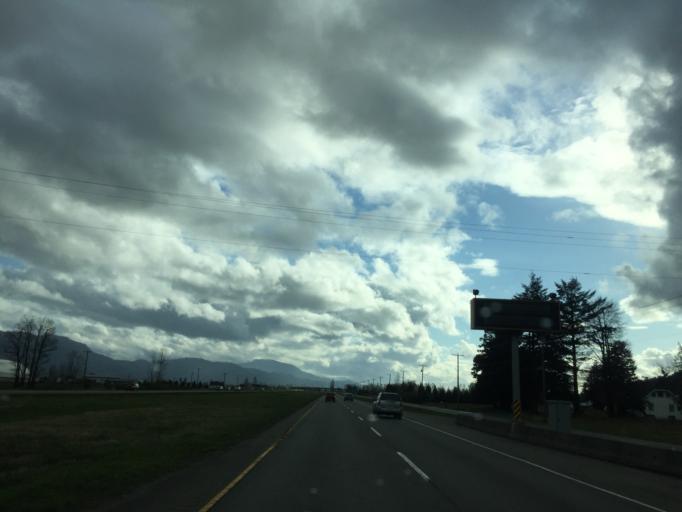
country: CA
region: British Columbia
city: Abbotsford
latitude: 49.0997
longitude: -122.1174
